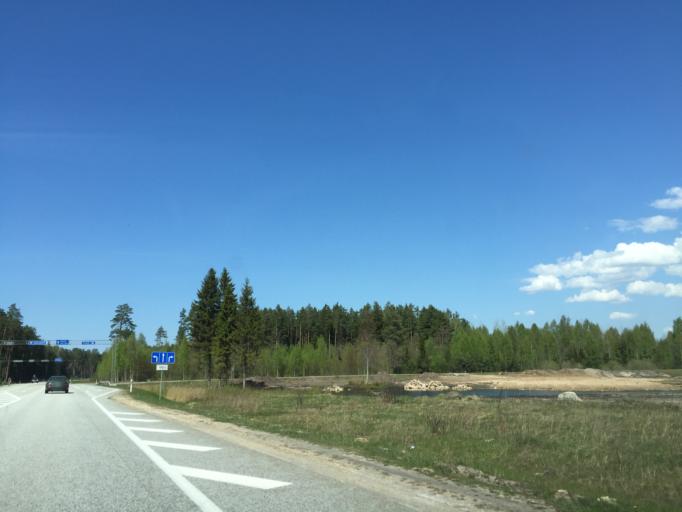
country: LV
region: Saulkrastu
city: Saulkrasti
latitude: 57.3417
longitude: 24.4462
